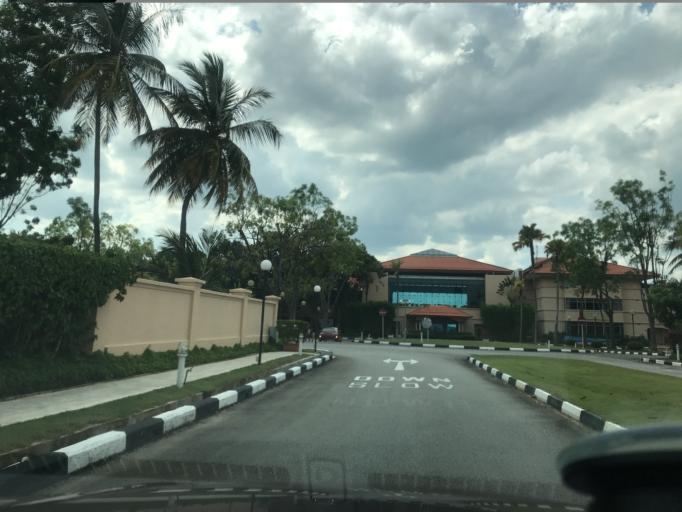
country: MY
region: Johor
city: Johor Bahru
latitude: 1.3422
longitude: 103.6364
